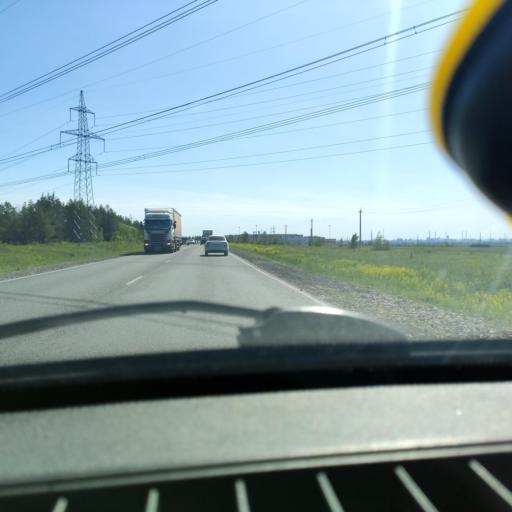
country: RU
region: Samara
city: Zhigulevsk
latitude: 53.5761
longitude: 49.5588
